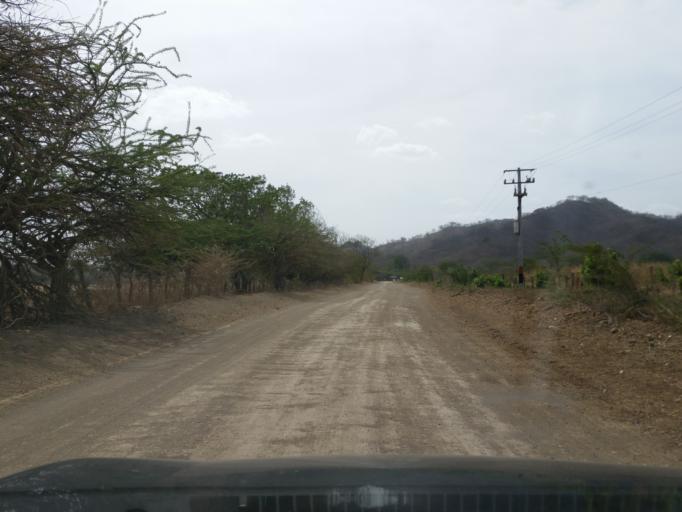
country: NI
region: Rivas
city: Tola
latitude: 11.4332
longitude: -86.0220
